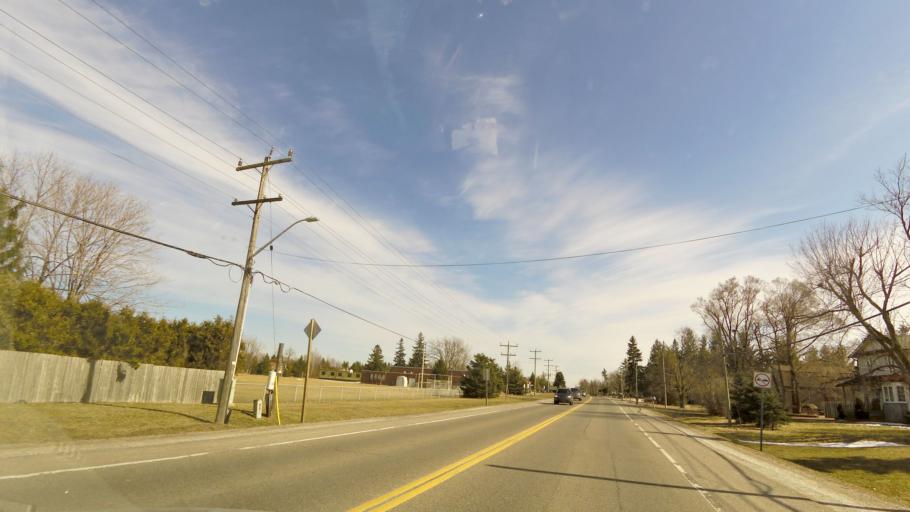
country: CA
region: Ontario
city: Burlington
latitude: 43.3595
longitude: -79.9341
